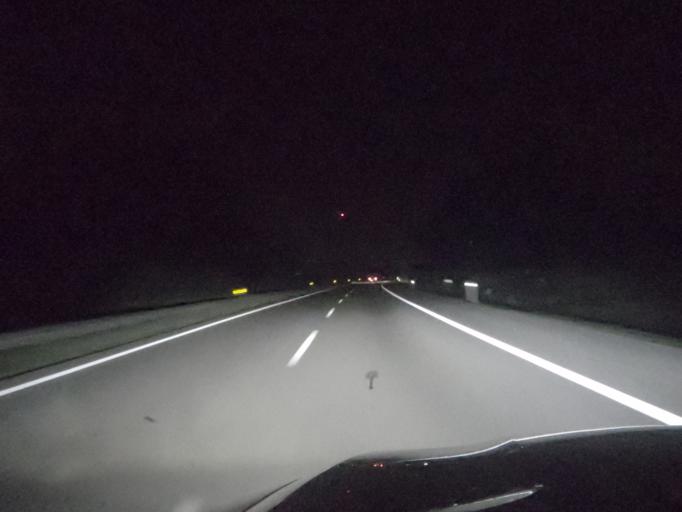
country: PT
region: Aveiro
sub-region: Oliveira do Bairro
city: Oliveira do Bairro
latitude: 40.4678
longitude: -8.5212
